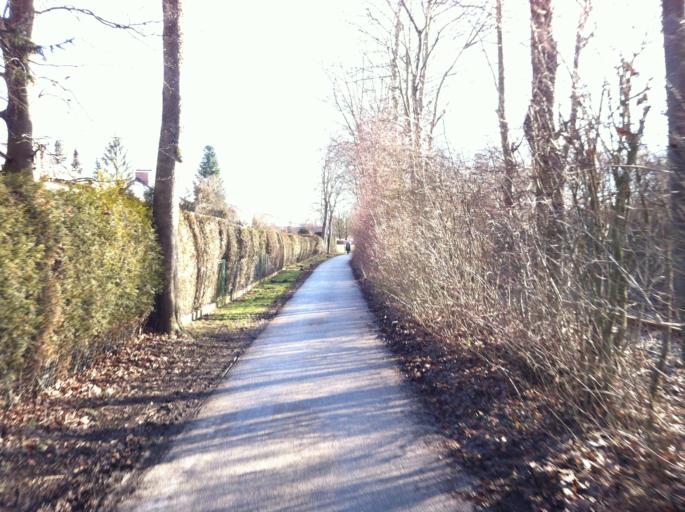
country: DE
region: Bavaria
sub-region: Upper Bavaria
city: Wolfratshausen
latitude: 47.9012
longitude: 11.4377
